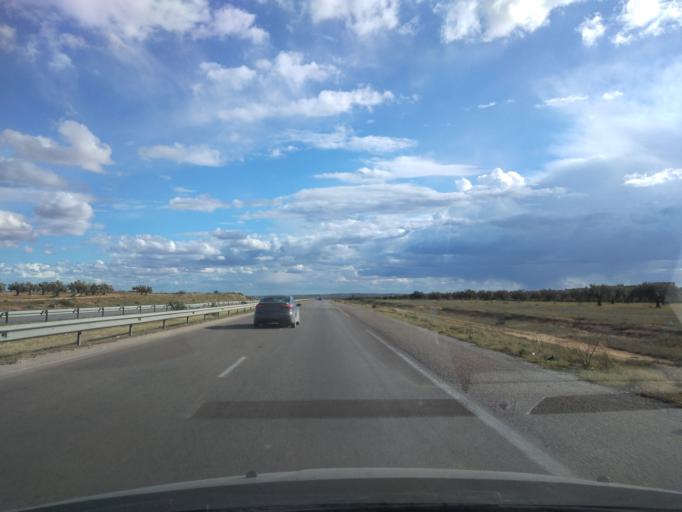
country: TN
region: Al Munastir
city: Manzil Kamil
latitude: 35.6128
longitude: 10.5966
